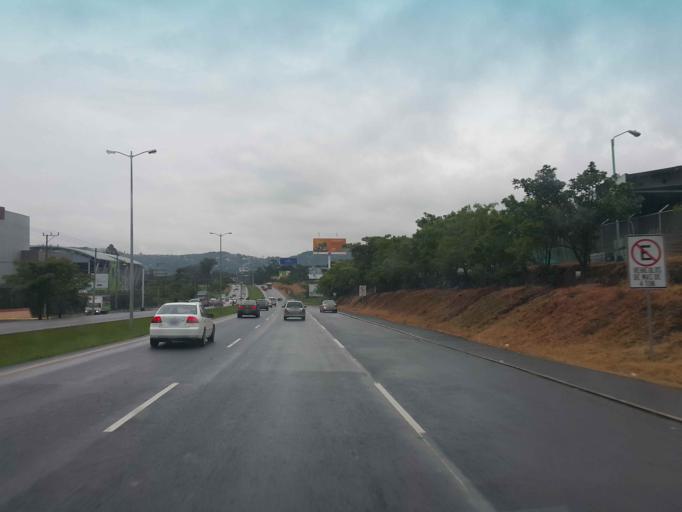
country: CR
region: San Jose
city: Santa Ana
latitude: 9.9369
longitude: -84.2135
